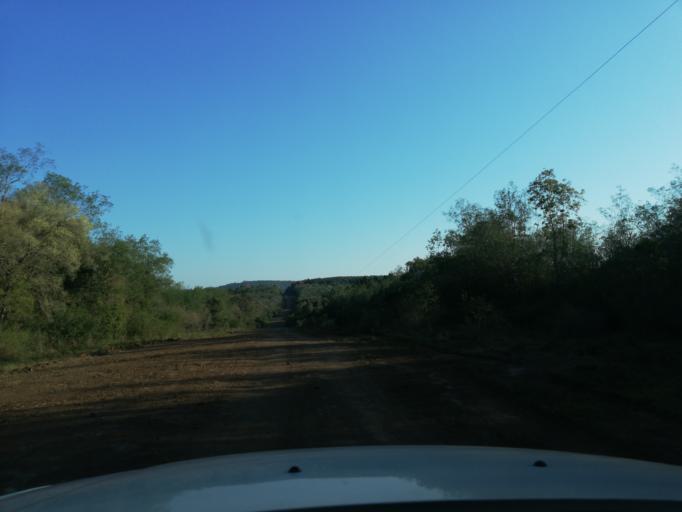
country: AR
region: Misiones
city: Cerro Cora
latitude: -27.5891
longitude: -55.6906
